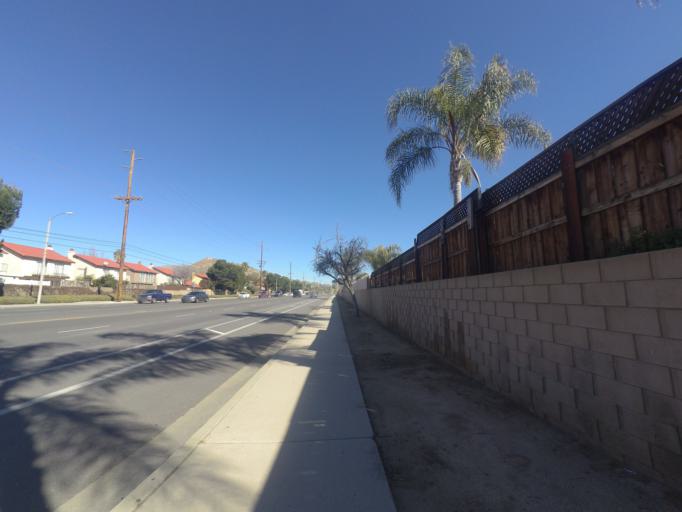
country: US
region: California
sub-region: Riverside County
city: Moreno Valley
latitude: 33.9288
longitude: -117.2611
